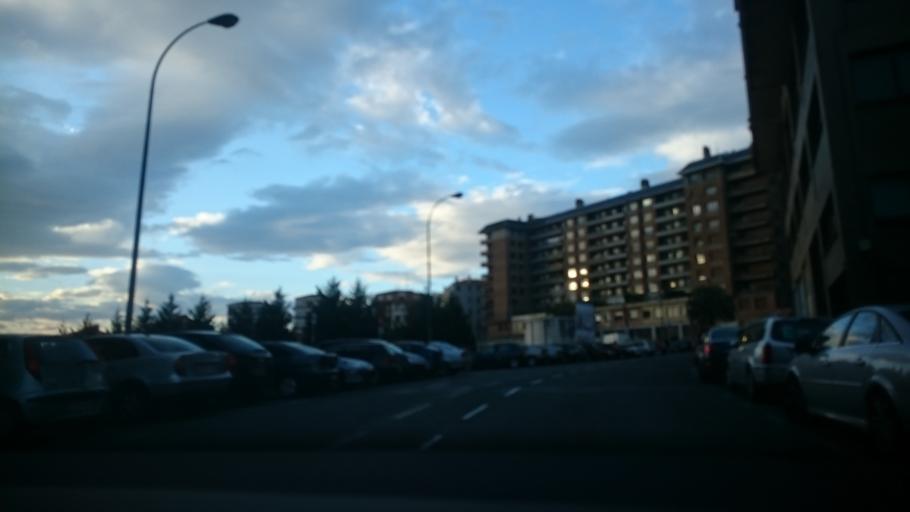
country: ES
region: Basque Country
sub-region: Bizkaia
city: Santutxu
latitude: 43.2583
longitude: -2.9174
